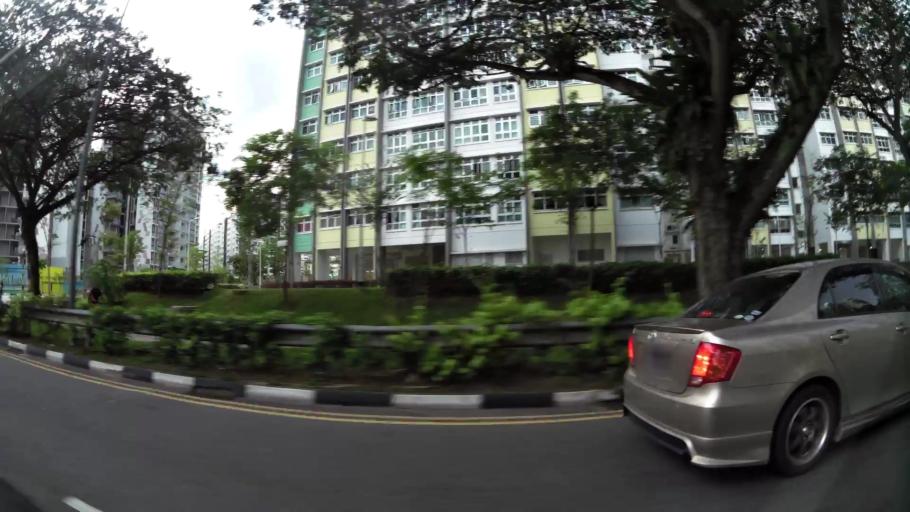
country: MY
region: Johor
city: Kampung Pasir Gudang Baru
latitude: 1.4188
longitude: 103.8470
